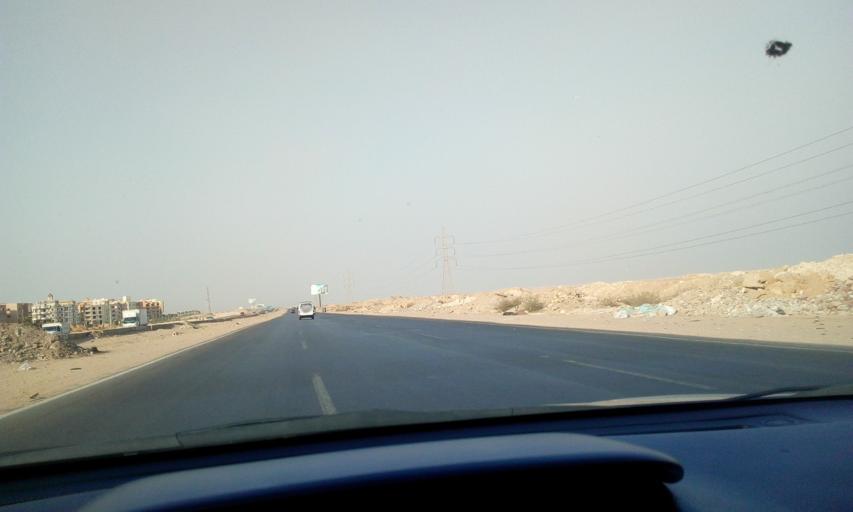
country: EG
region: Al Jizah
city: Madinat Sittah Uktubar
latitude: 29.8906
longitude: 31.0819
